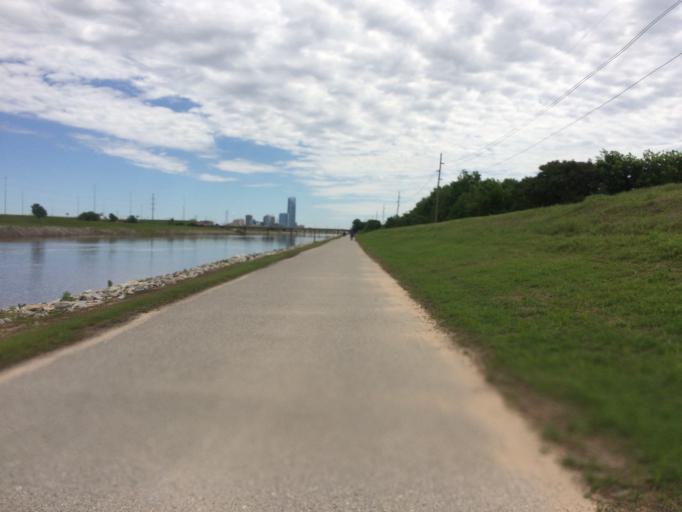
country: US
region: Oklahoma
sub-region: Oklahoma County
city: Oklahoma City
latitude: 35.4576
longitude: -97.5632
